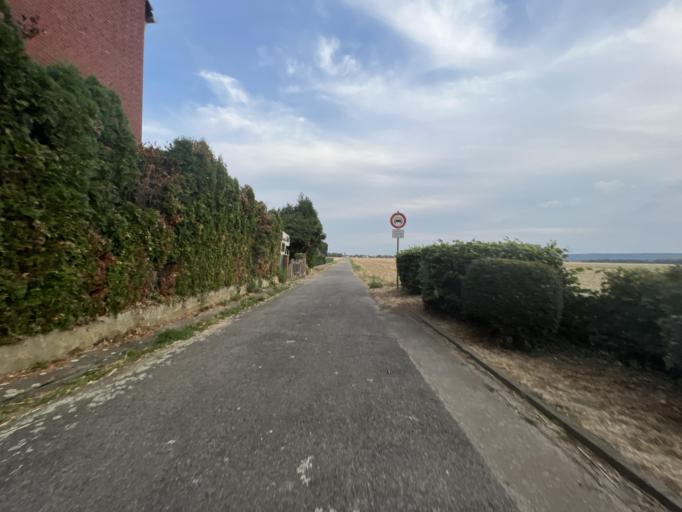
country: DE
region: North Rhine-Westphalia
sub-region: Regierungsbezirk Koln
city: Dueren
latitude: 50.8287
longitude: 6.4351
